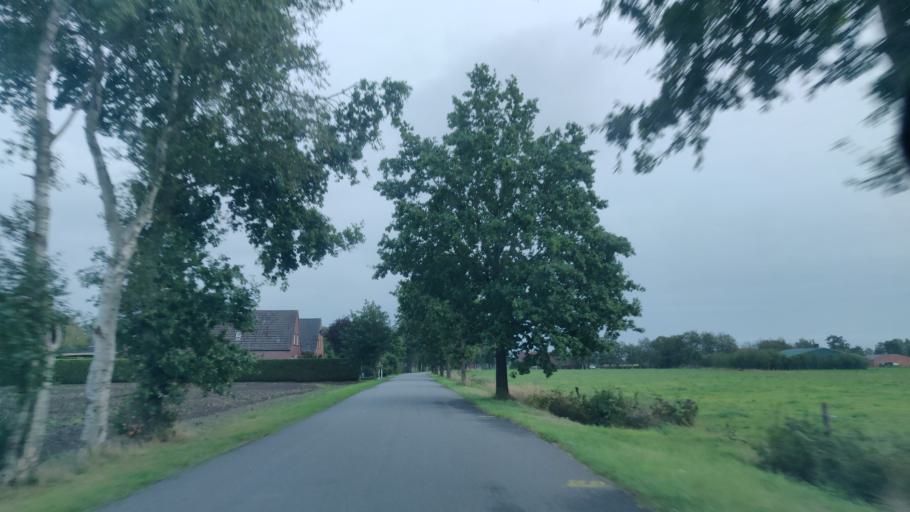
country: DE
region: Lower Saxony
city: Aurich
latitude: 53.4955
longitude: 7.4379
